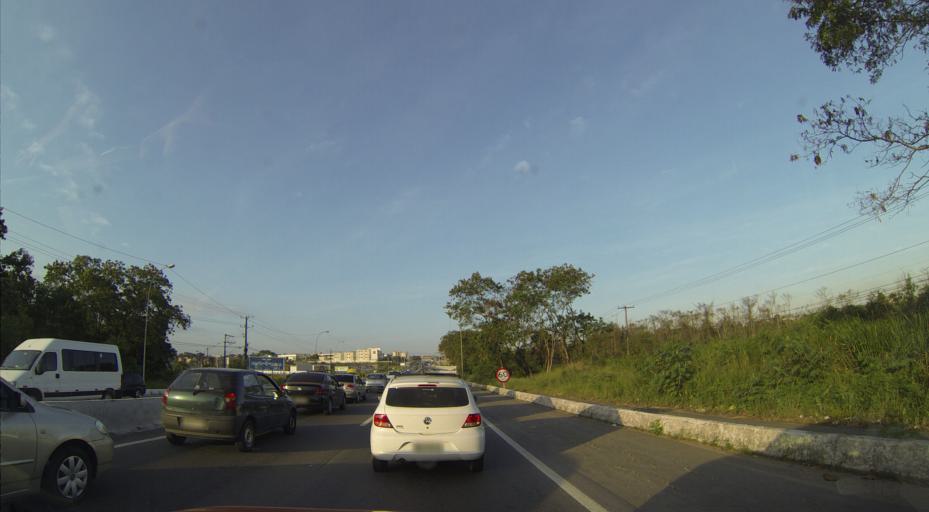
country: BR
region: Espirito Santo
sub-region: Vila Velha
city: Vila Velha
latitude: -20.2419
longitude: -40.2806
